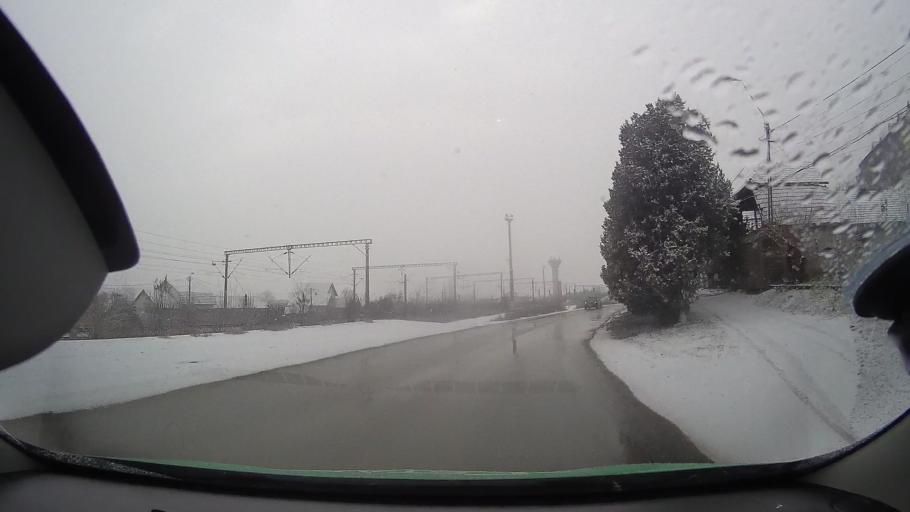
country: RO
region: Alba
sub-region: Municipiul Aiud
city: Aiud
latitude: 46.3096
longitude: 23.7352
